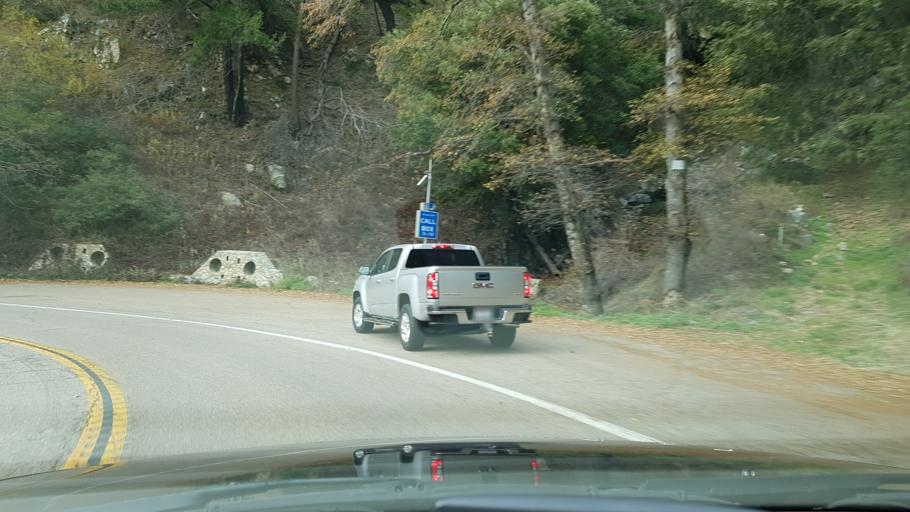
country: US
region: California
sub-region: Riverside County
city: Aguanga
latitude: 33.3063
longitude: -116.8773
